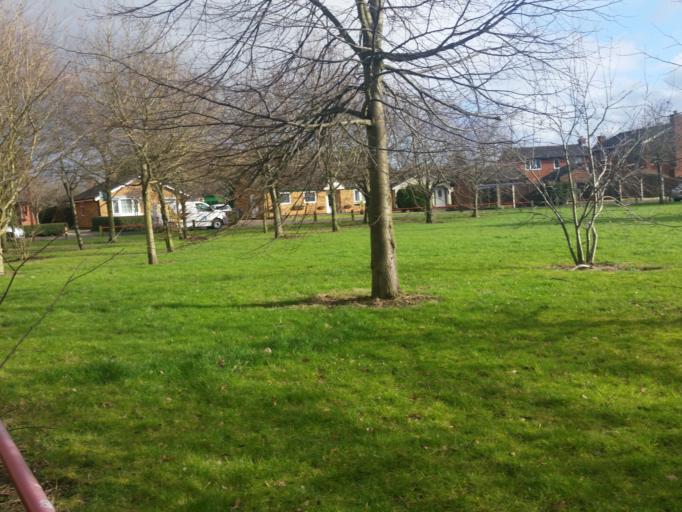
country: GB
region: England
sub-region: Derbyshire
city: Borrowash
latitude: 52.8969
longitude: -1.4169
